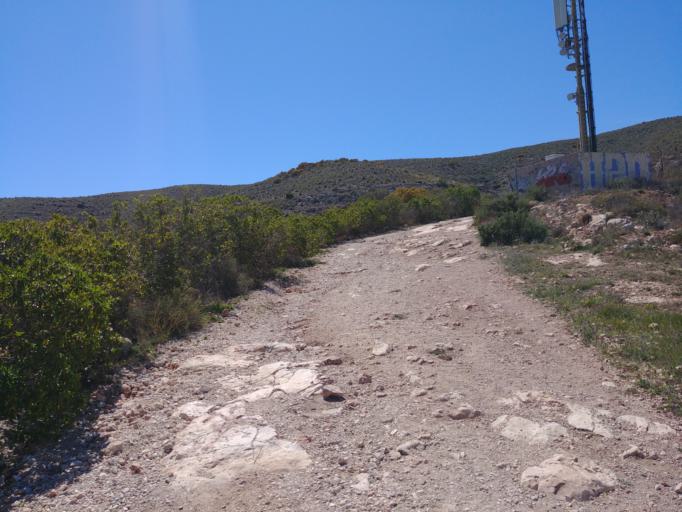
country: ES
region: Andalusia
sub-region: Provincia de Almeria
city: Carboneras
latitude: 36.9407
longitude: -1.9395
